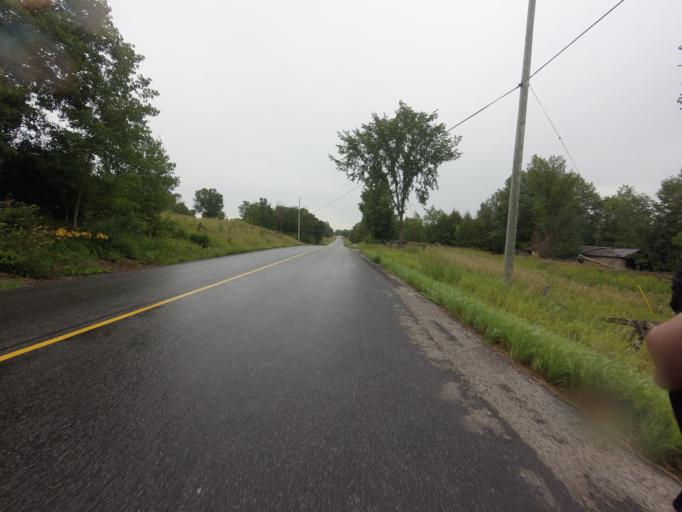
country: CA
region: Ontario
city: Perth
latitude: 44.9400
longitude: -76.4363
